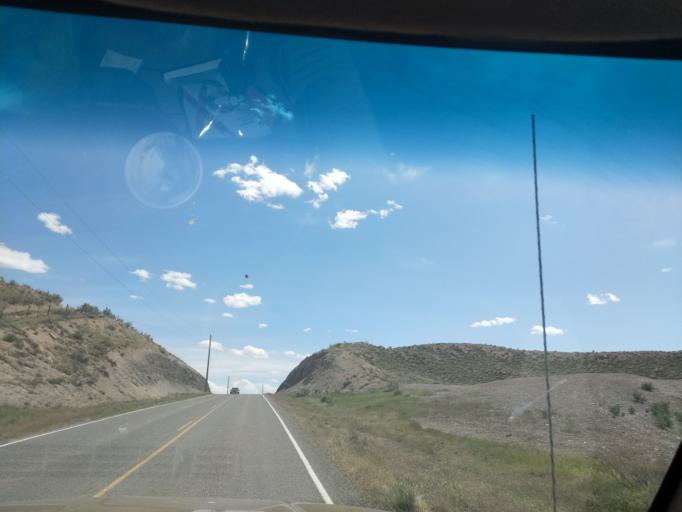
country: US
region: Colorado
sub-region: Mesa County
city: Fruita
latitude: 39.2086
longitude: -108.7570
